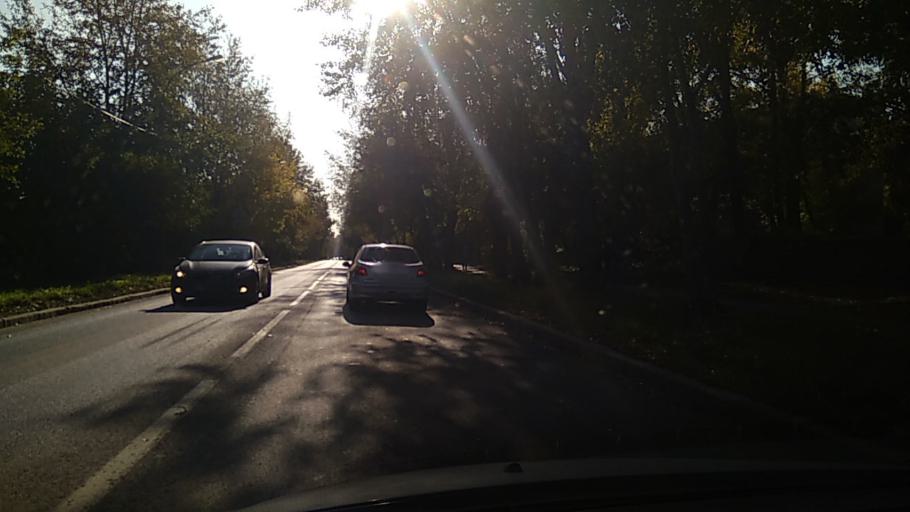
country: RU
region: Sverdlovsk
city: Yekaterinburg
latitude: 56.7765
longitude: 60.6389
